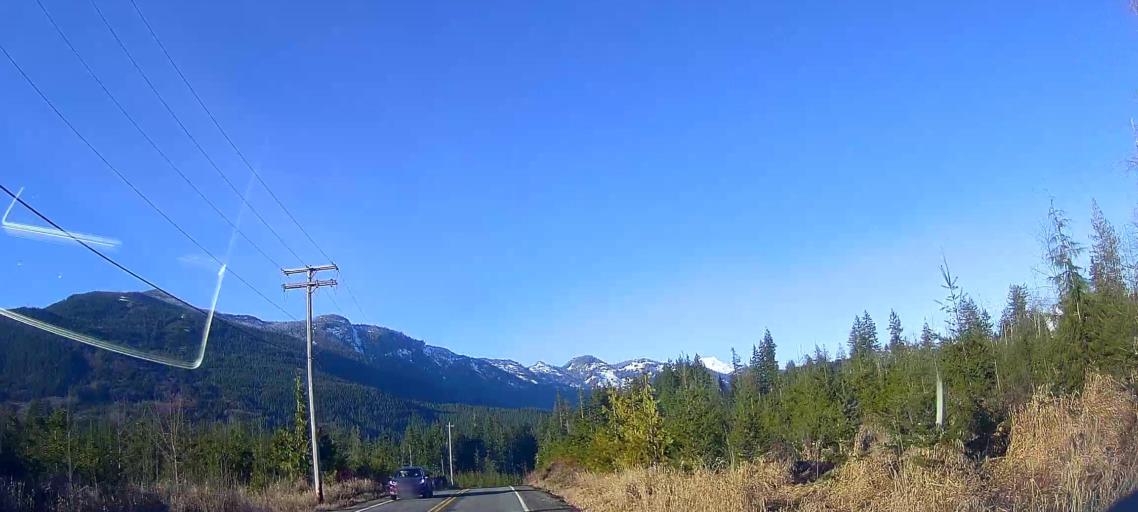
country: US
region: Washington
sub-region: Snohomish County
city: Darrington
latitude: 48.5696
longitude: -121.7684
